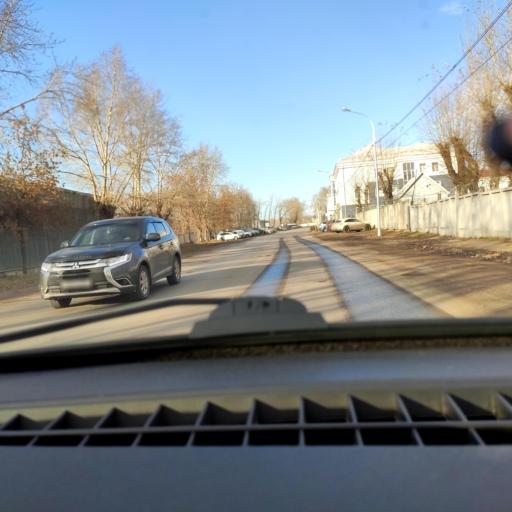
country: RU
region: Bashkortostan
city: Ufa
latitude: 54.8401
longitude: 56.0795
